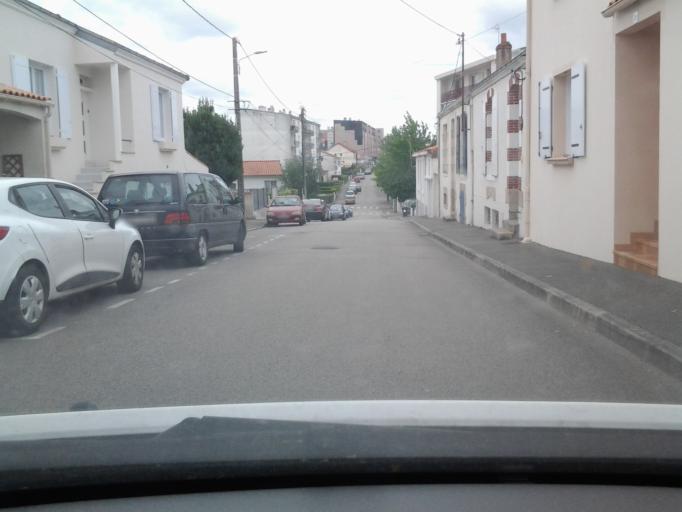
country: FR
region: Pays de la Loire
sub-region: Departement de la Vendee
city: La Roche-sur-Yon
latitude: 46.6661
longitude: -1.4339
